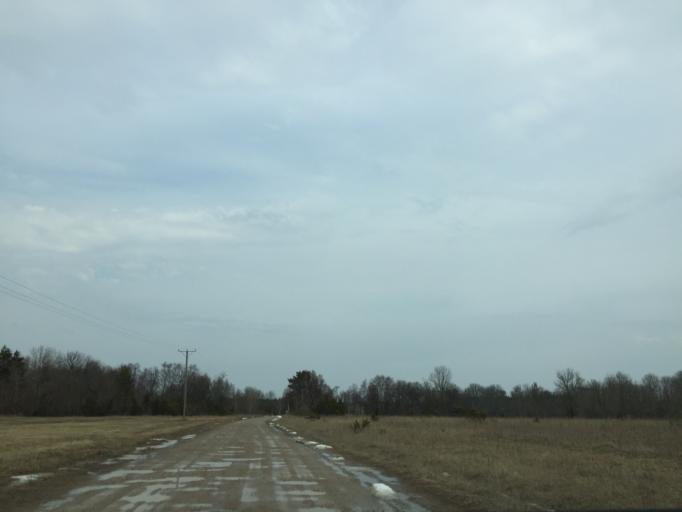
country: EE
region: Saare
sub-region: Kuressaare linn
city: Kuressaare
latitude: 58.4370
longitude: 22.1447
